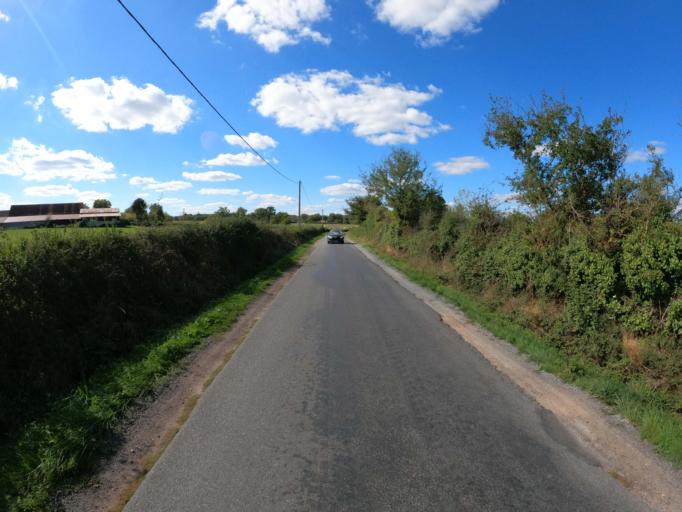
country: FR
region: Auvergne
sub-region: Departement de l'Allier
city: Doyet
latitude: 46.3900
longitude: 2.7609
